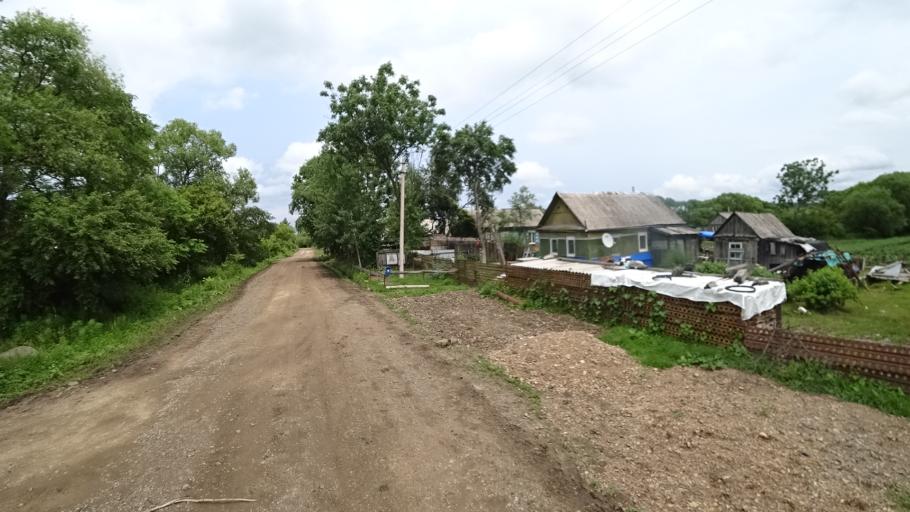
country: RU
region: Primorskiy
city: Novosysoyevka
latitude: 44.2270
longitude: 133.3734
